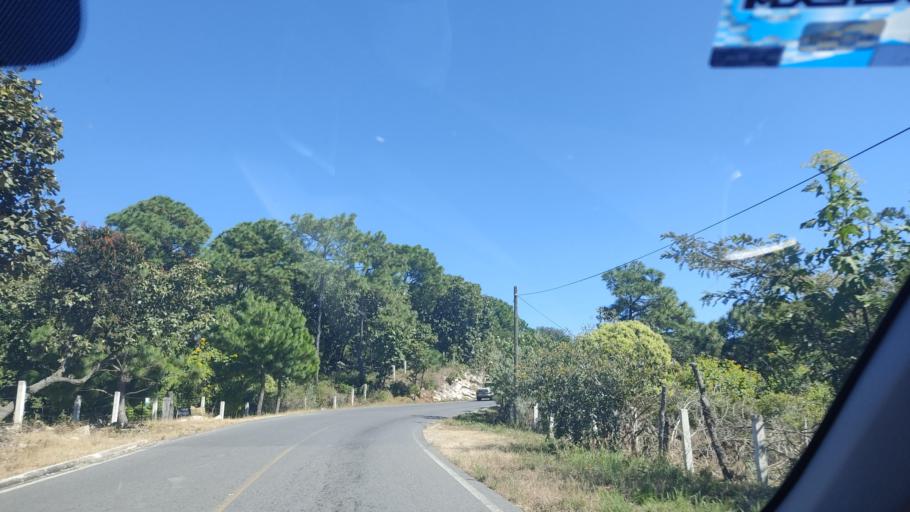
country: MX
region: Nayarit
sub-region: Jala
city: Rosa Blanca
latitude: 21.0996
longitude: -104.3685
